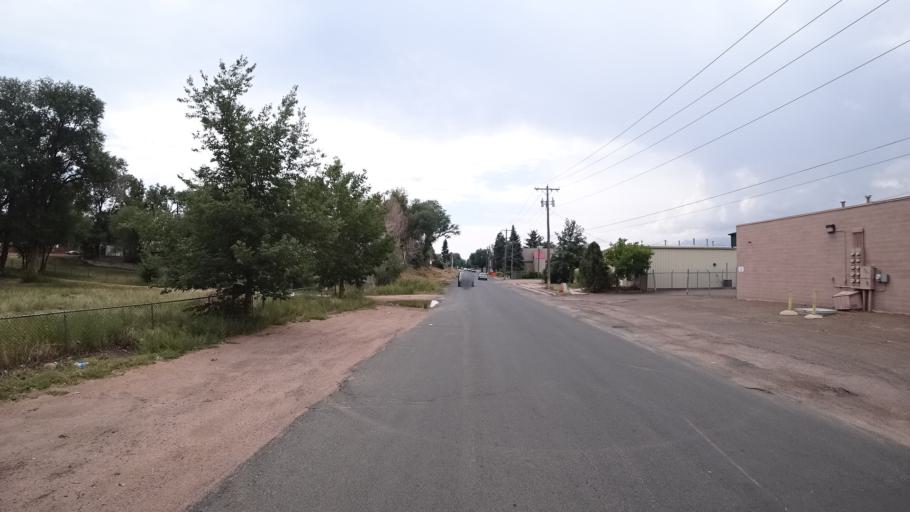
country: US
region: Colorado
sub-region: El Paso County
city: Colorado Springs
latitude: 38.8772
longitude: -104.8269
